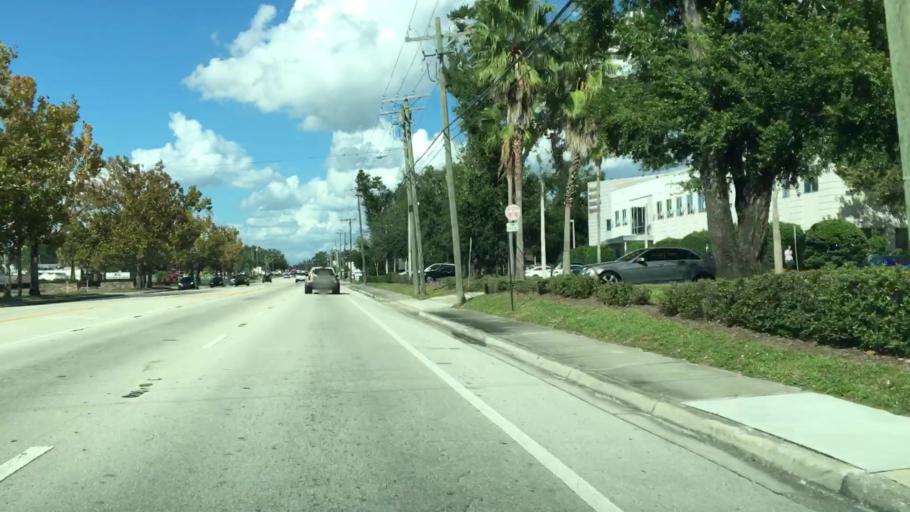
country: US
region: Florida
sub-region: Orange County
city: Edgewood
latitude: 28.4872
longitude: -81.3726
